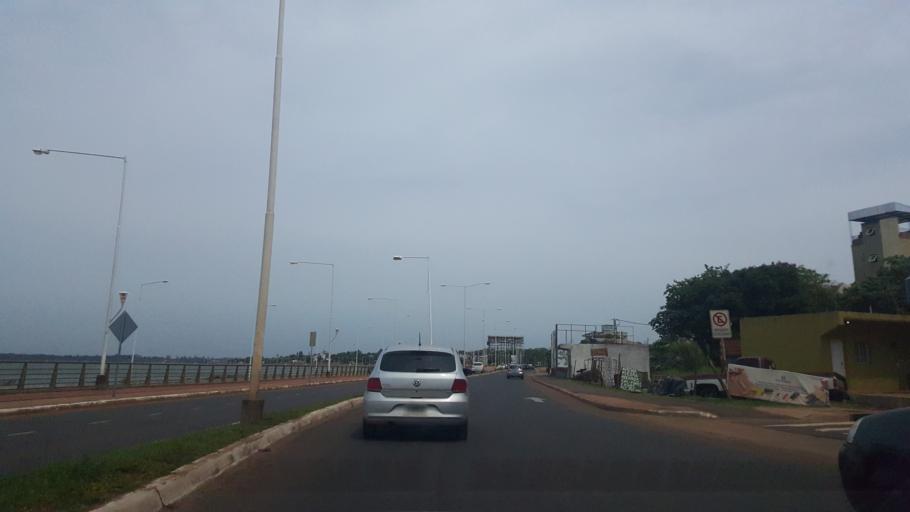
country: AR
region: Misiones
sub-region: Departamento de Capital
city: Posadas
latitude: -27.3879
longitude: -55.8891
